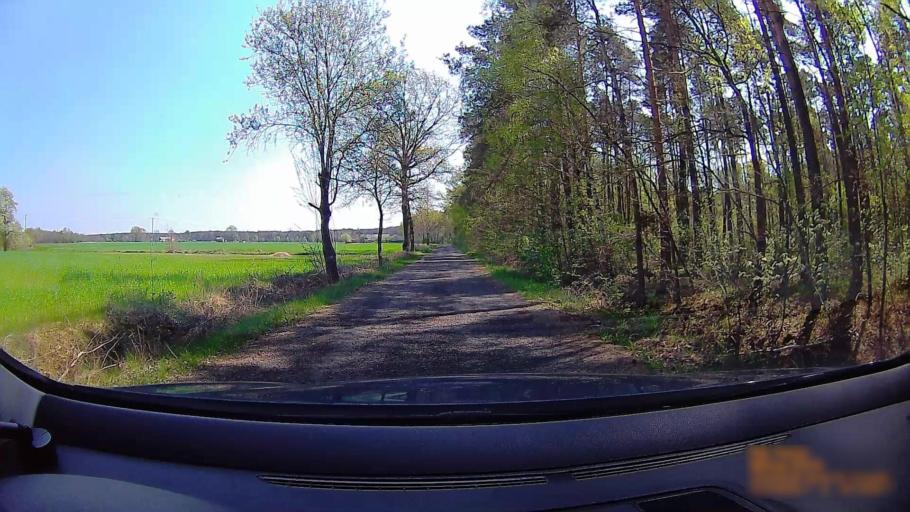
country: PL
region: Greater Poland Voivodeship
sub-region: Powiat koninski
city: Rychwal
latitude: 52.0933
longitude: 18.1741
